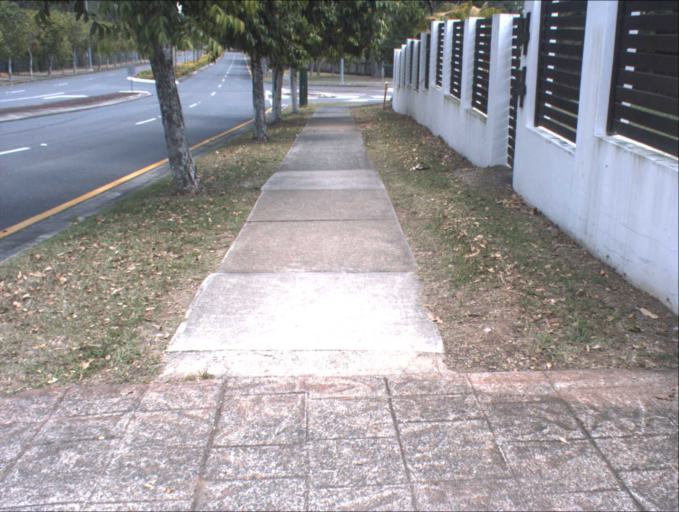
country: AU
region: Queensland
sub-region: Logan
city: Slacks Creek
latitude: -27.6384
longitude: 153.1466
